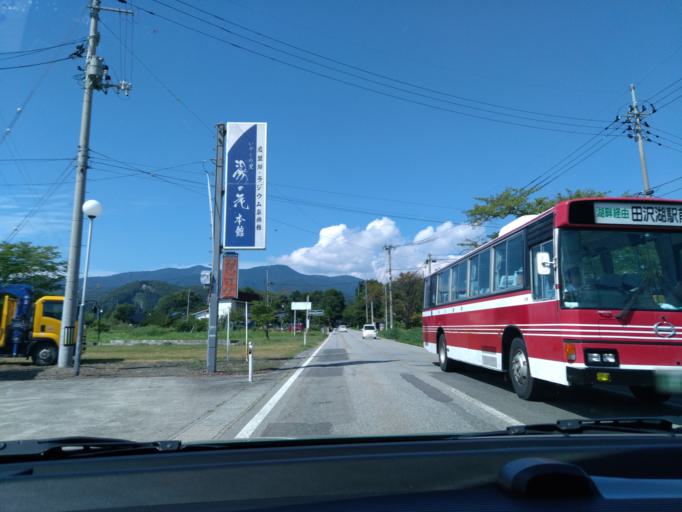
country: JP
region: Akita
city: Kakunodatemachi
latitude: 39.7443
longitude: 140.7203
